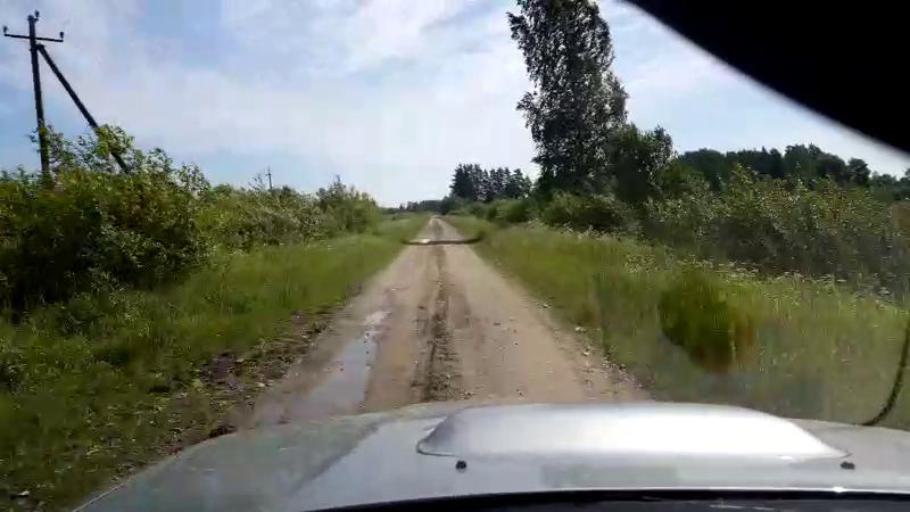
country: EE
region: Paernumaa
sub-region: Sindi linn
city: Sindi
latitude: 58.5196
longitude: 24.6721
